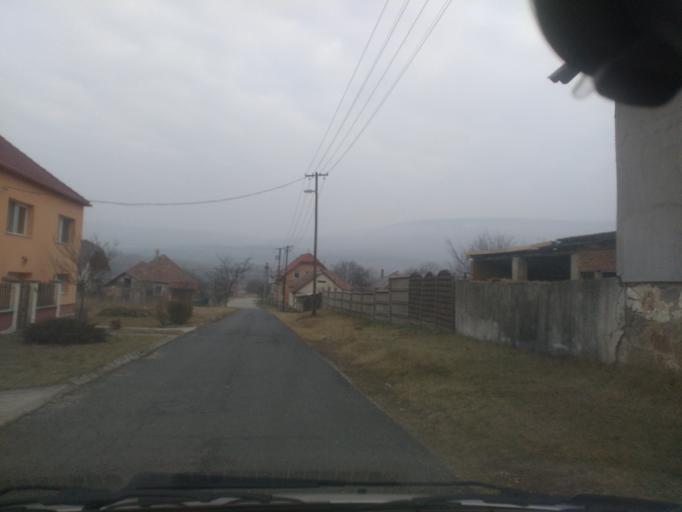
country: HU
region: Komarom-Esztergom
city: Piliscsev
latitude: 47.6739
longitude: 18.8111
